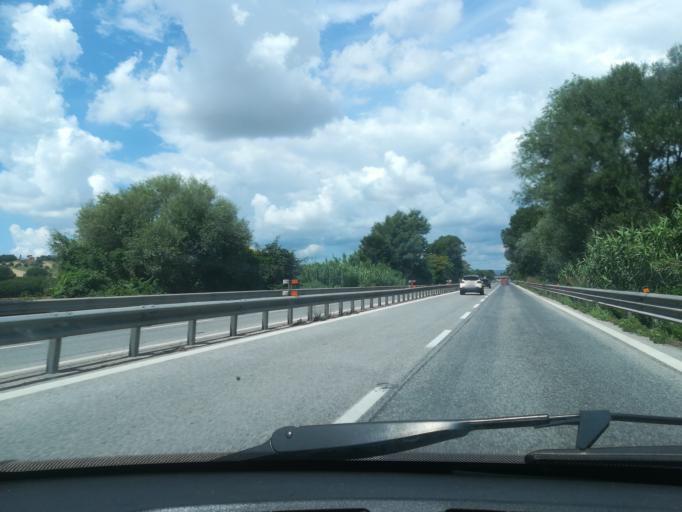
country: IT
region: The Marches
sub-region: Provincia di Macerata
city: Villa San Filippo
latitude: 43.2635
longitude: 13.5564
